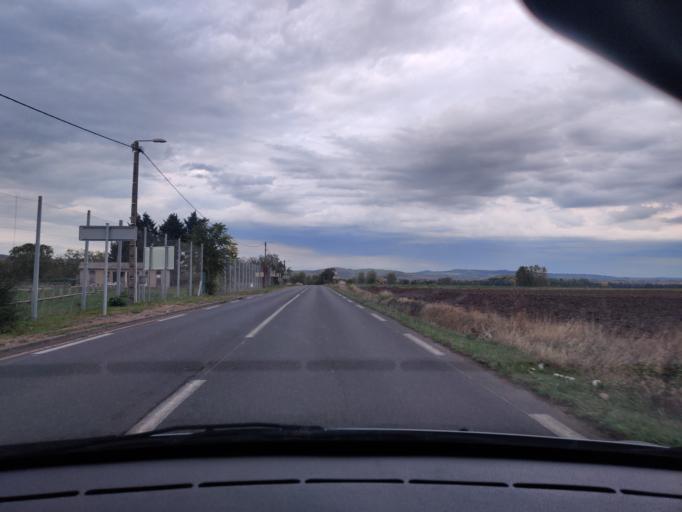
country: FR
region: Auvergne
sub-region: Departement du Puy-de-Dome
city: Saint-Bonnet-pres-Riom
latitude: 45.9352
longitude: 3.1114
